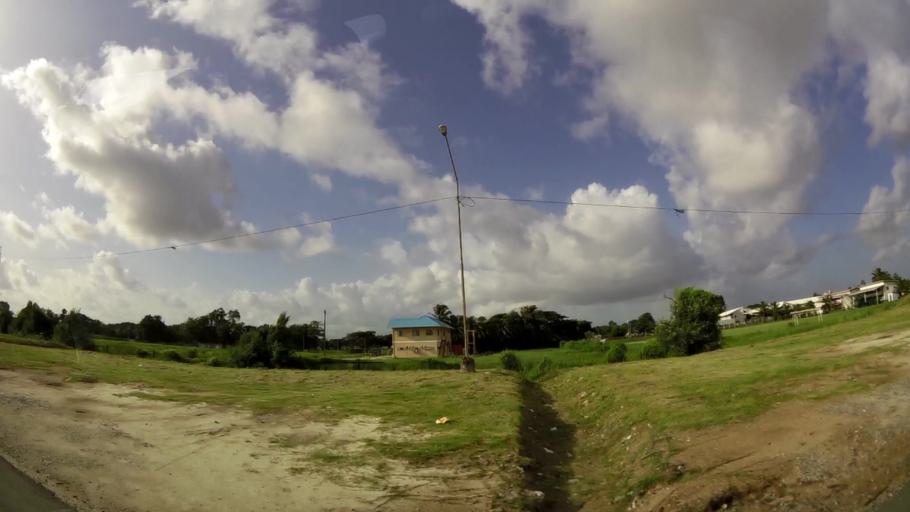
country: GY
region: Demerara-Mahaica
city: Georgetown
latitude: 6.8247
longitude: -58.1537
